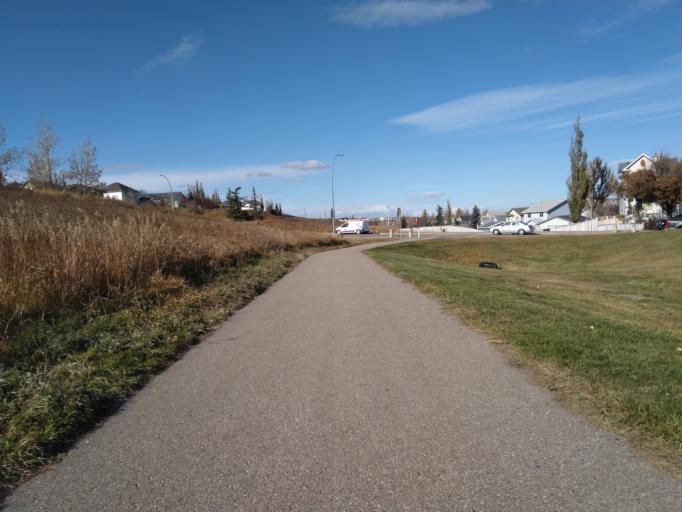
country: CA
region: Alberta
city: Calgary
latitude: 51.1510
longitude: -114.1129
